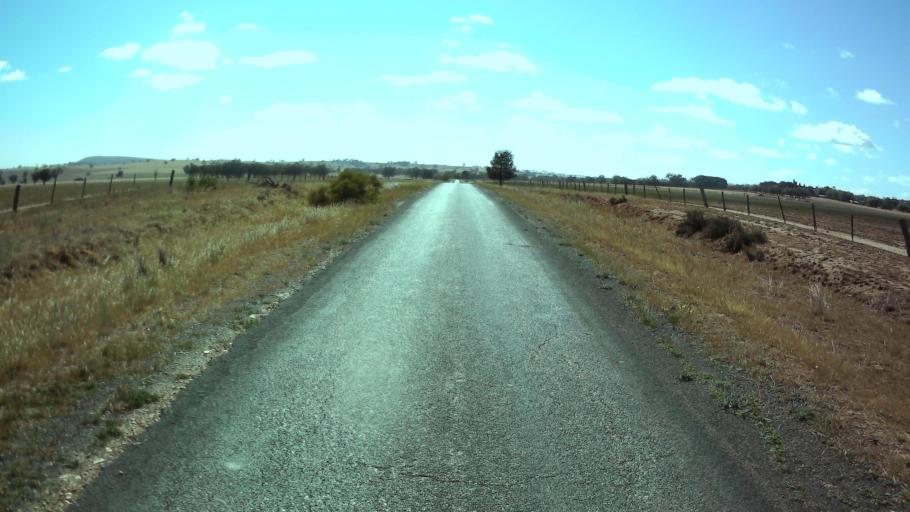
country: AU
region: New South Wales
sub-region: Young
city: Young
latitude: -34.0753
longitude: 148.3532
